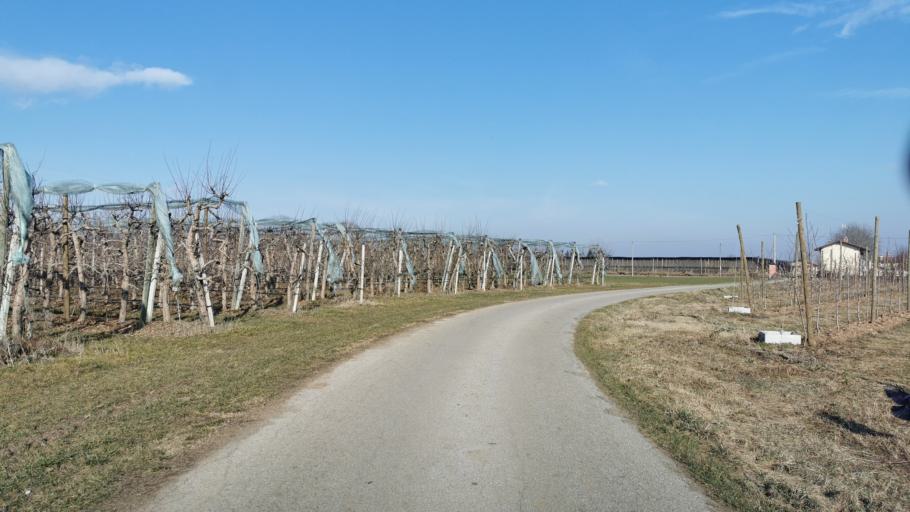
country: IT
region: Piedmont
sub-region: Provincia di Cuneo
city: Caraglio
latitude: 44.4464
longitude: 7.4473
